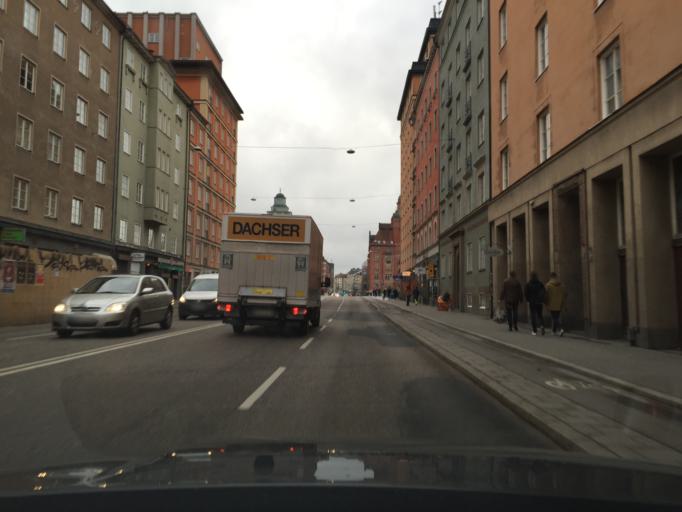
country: SE
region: Stockholm
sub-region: Stockholms Kommun
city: Stockholm
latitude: 59.3387
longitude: 18.0359
